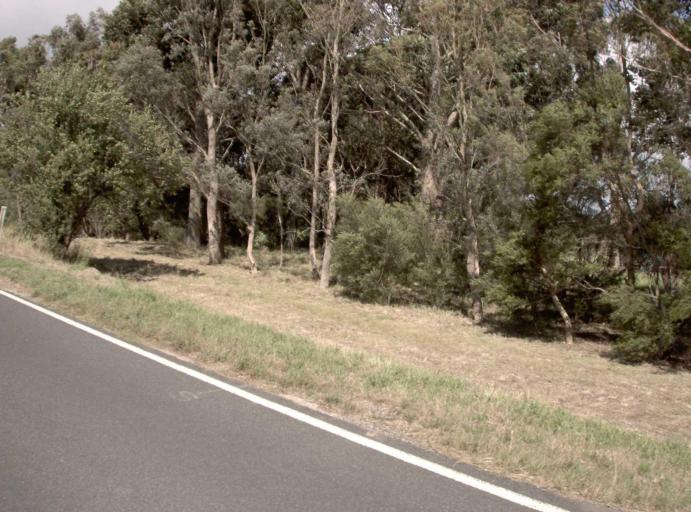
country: AU
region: Victoria
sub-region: Latrobe
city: Traralgon
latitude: -38.1531
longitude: 146.5207
